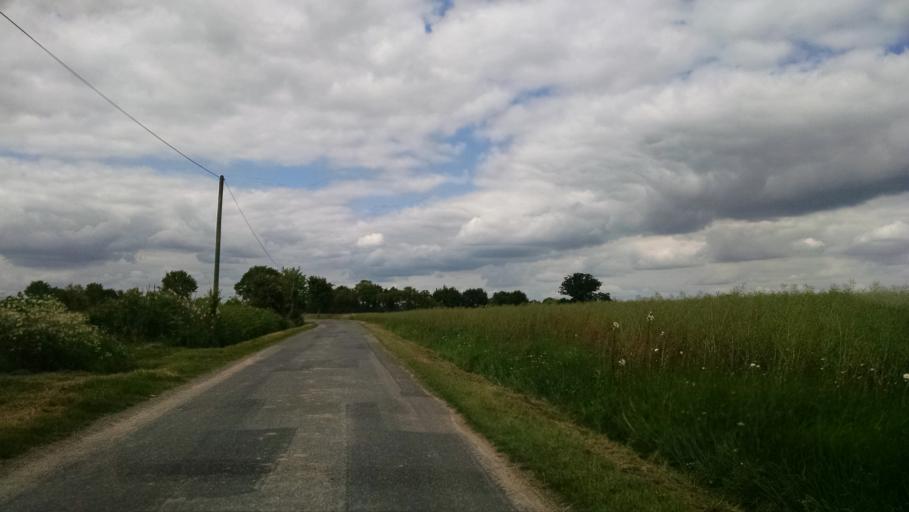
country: FR
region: Pays de la Loire
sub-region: Departement de la Loire-Atlantique
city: Remouille
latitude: 47.0126
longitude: -1.3741
